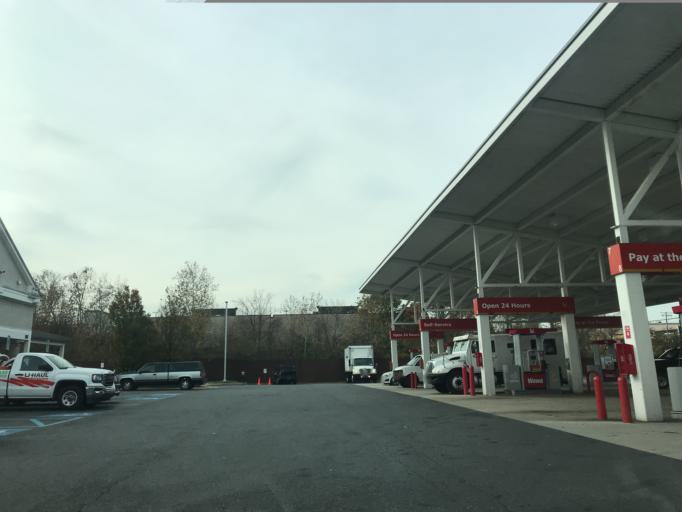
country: US
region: Maryland
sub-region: Baltimore County
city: Rossville
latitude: 39.3363
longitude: -76.4815
